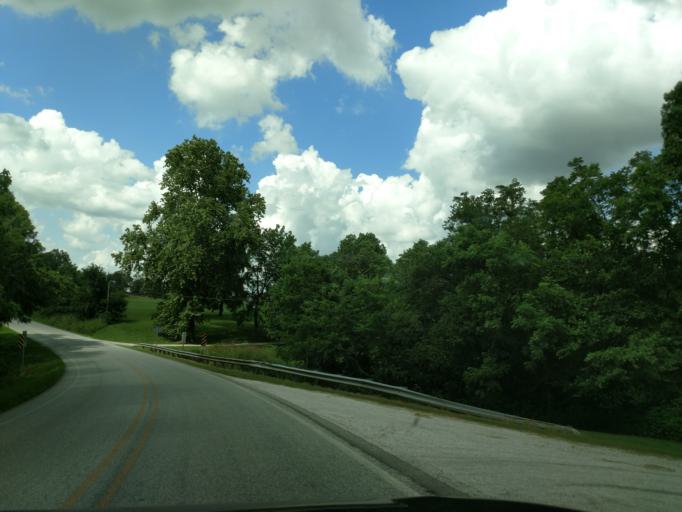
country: US
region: Arkansas
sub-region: Carroll County
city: Berryville
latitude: 36.4079
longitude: -93.5617
